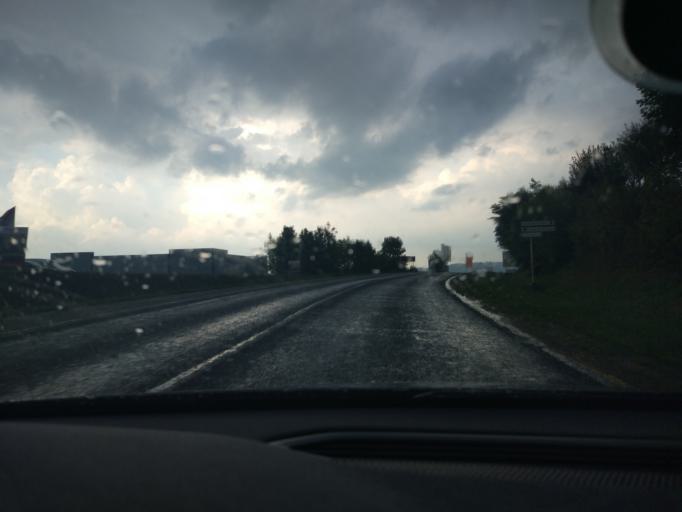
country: FR
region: Lorraine
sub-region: Departement de la Meuse
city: Belleville-sur-Meuse
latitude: 49.1808
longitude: 5.3689
